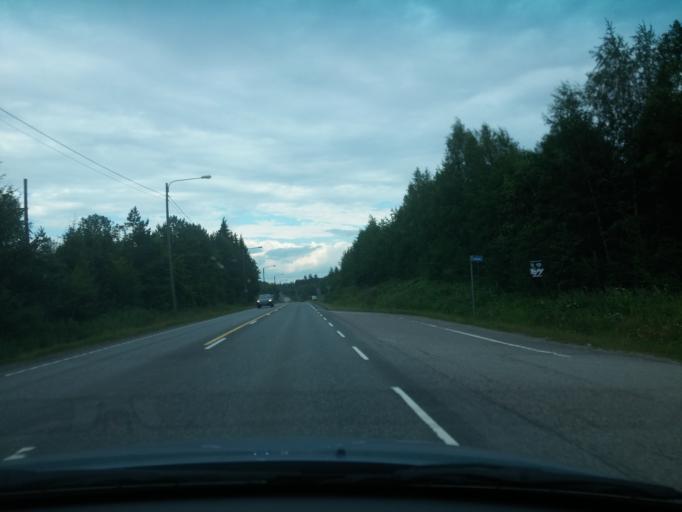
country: FI
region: Haeme
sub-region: Riihimaeki
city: Loppi
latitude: 60.7260
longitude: 24.5141
